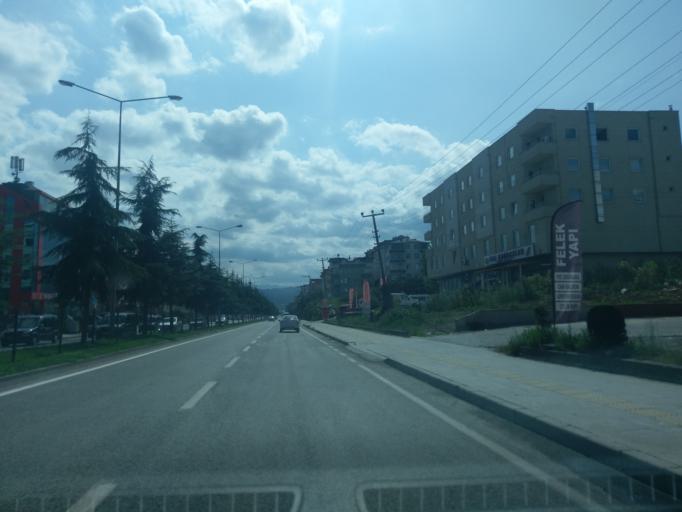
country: TR
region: Ordu
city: Ordu
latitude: 40.9645
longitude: 37.8999
